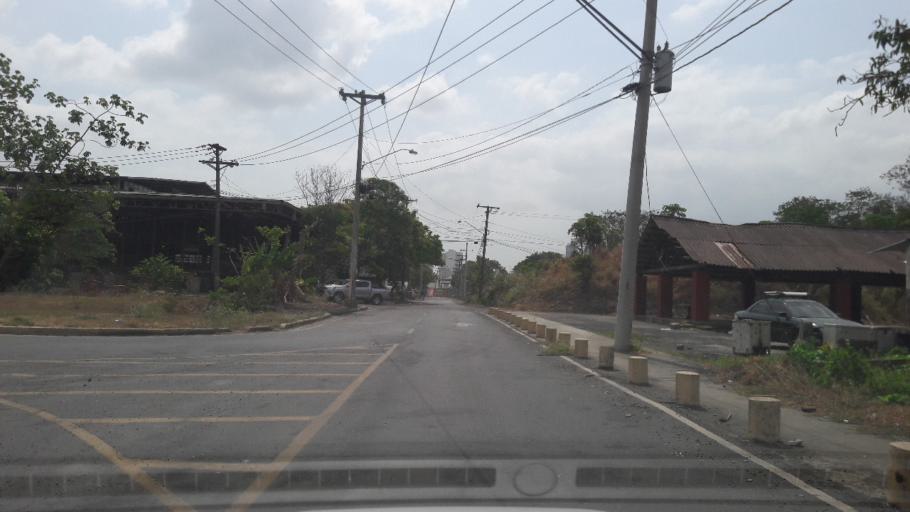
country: PA
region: Panama
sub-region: Distrito de Panama
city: Ancon
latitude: 8.9718
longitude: -79.5496
